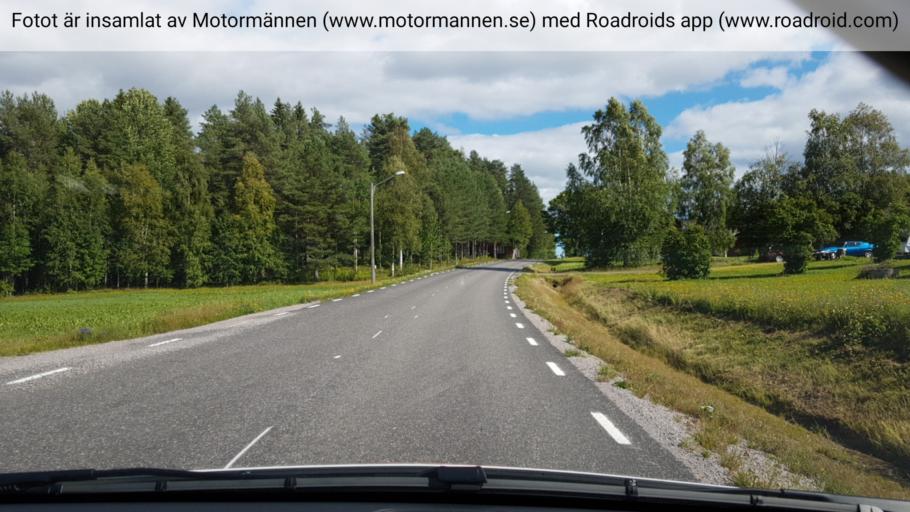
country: SE
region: Vaesterbotten
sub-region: Umea Kommun
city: Hoernefors
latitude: 63.7030
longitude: 19.8166
